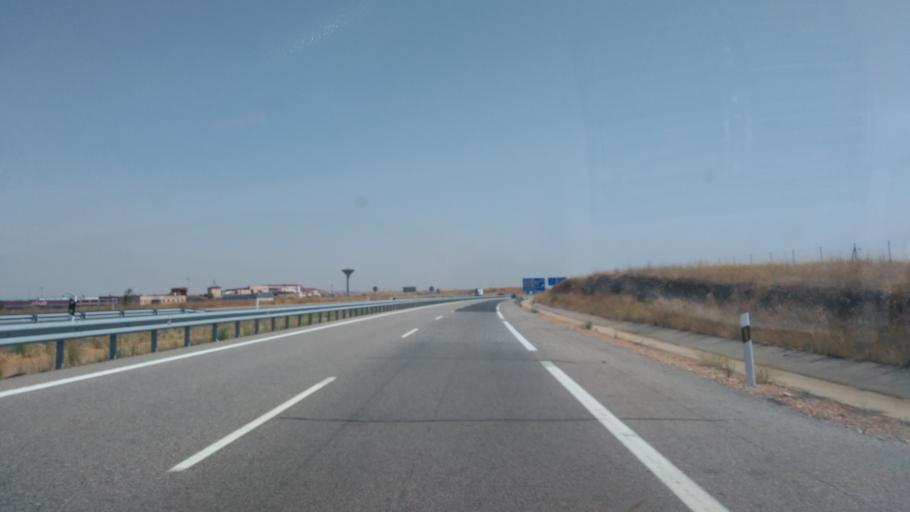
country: ES
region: Castille and Leon
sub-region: Provincia de Salamanca
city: Doninos de Salamanca
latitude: 40.9563
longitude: -5.7282
